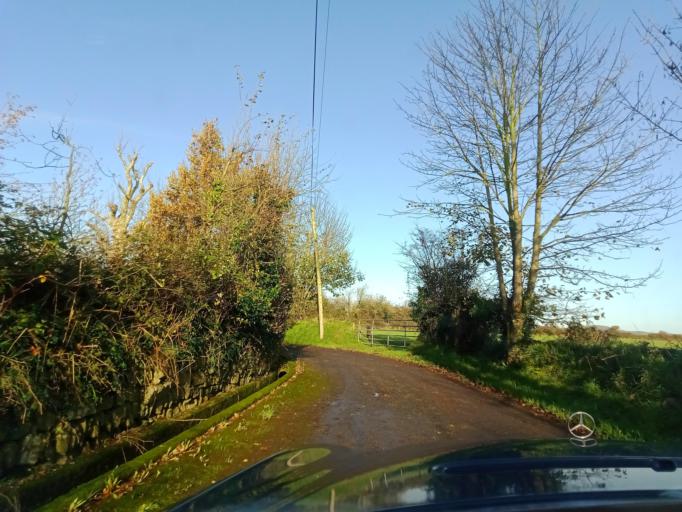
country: IE
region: Leinster
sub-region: Kilkenny
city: Mooncoin
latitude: 52.2931
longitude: -7.2062
